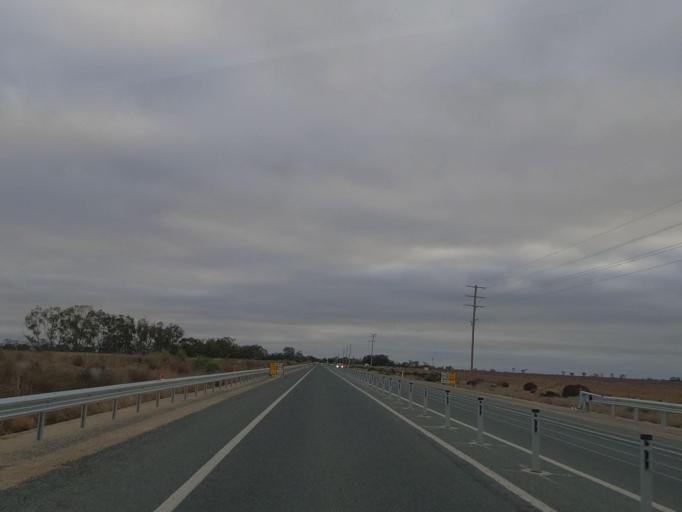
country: AU
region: Victoria
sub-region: Swan Hill
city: Swan Hill
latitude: -35.5416
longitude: 143.7542
